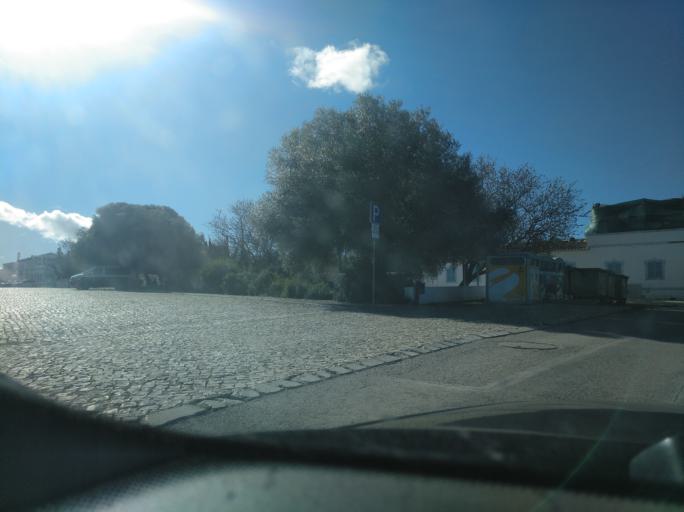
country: PT
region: Faro
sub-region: Vila Real de Santo Antonio
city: Monte Gordo
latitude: 37.1589
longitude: -7.5466
